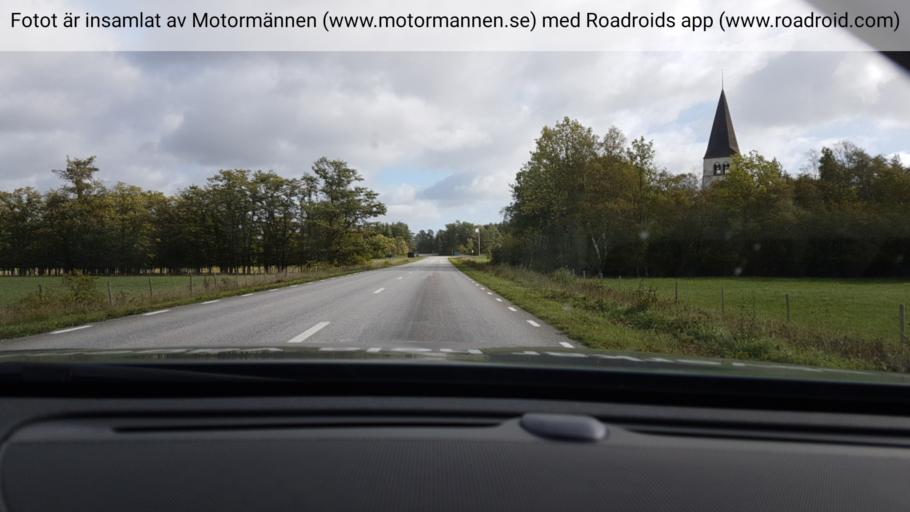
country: SE
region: Gotland
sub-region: Gotland
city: Slite
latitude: 57.8336
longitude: 18.9175
